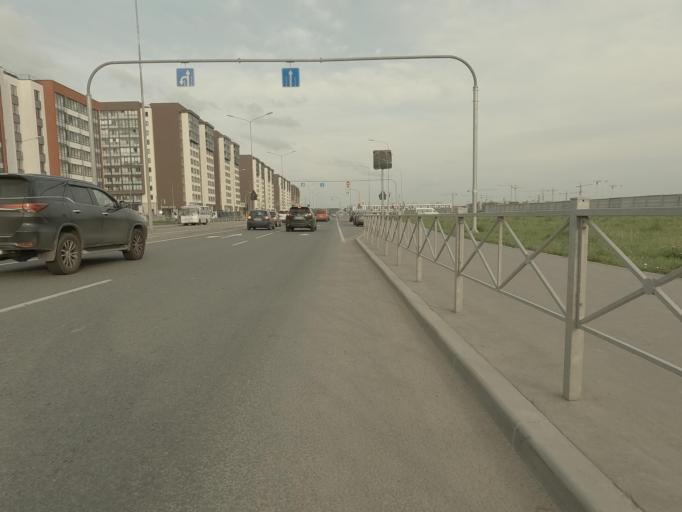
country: RU
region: St.-Petersburg
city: Sosnovaya Polyana
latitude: 59.8384
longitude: 30.1008
